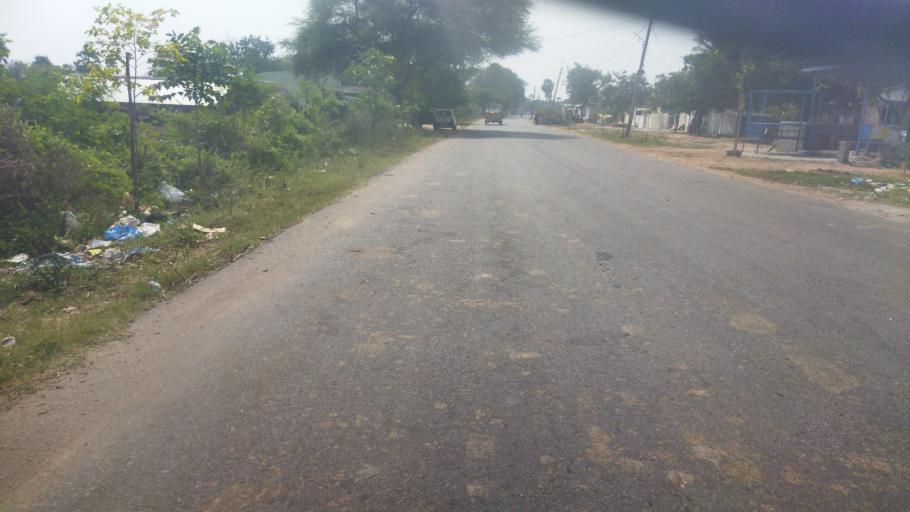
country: IN
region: Telangana
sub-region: Nalgonda
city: Nalgonda
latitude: 17.1507
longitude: 79.3104
